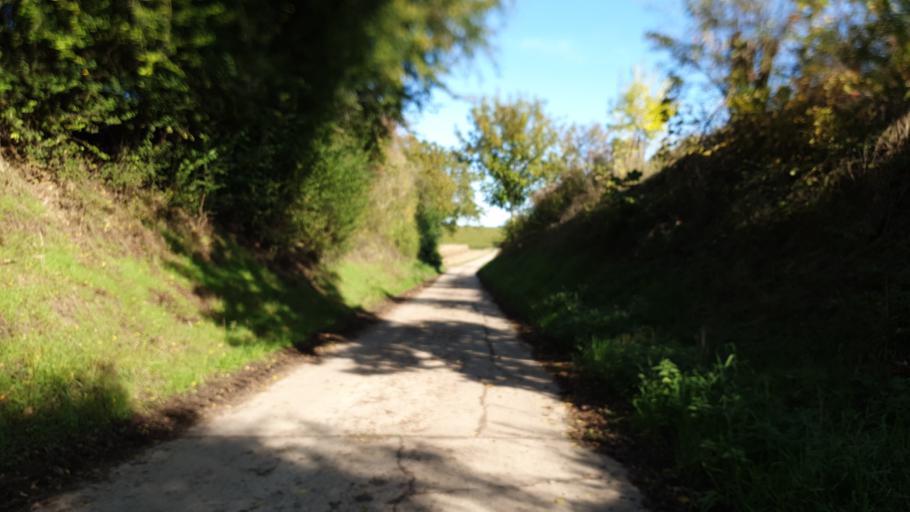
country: DE
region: Rheinland-Pfalz
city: Hergersweiler
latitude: 49.1149
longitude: 8.0911
